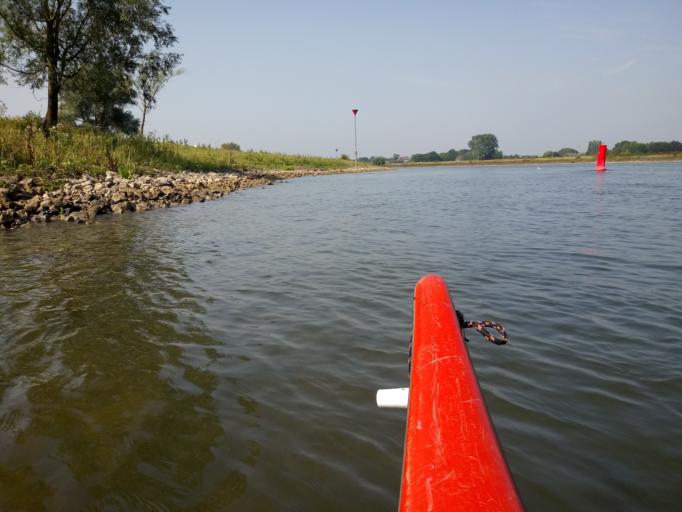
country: NL
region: Gelderland
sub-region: Gemeente Brummen
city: Brummen
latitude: 52.0910
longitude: 6.1821
